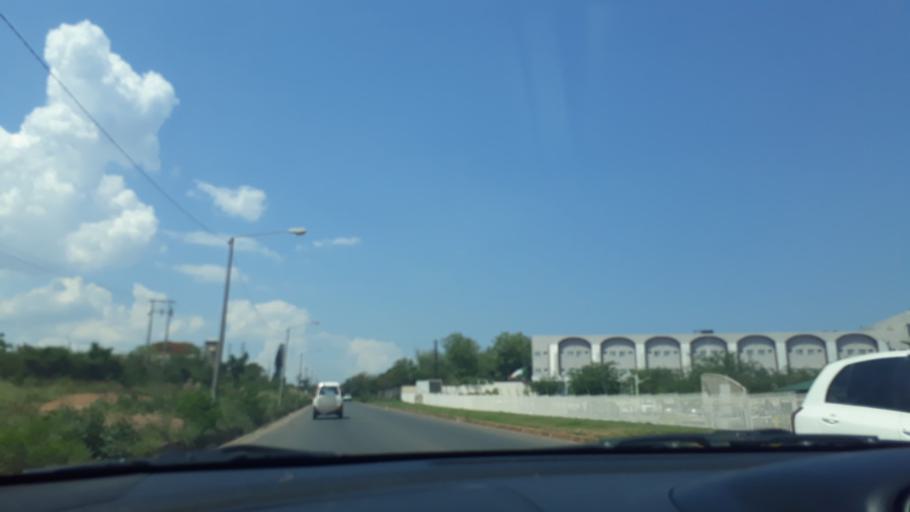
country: MZ
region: Maputo
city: Matola
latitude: -25.9655
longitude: 32.4456
